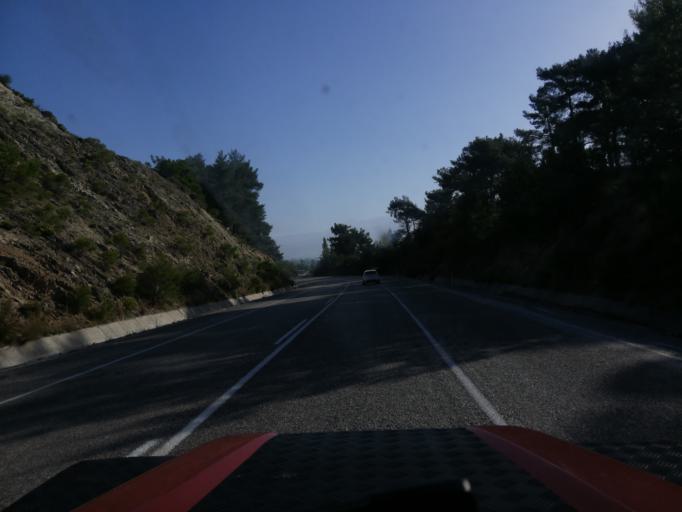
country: TR
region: Mugla
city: Esen
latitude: 36.4971
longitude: 29.3253
